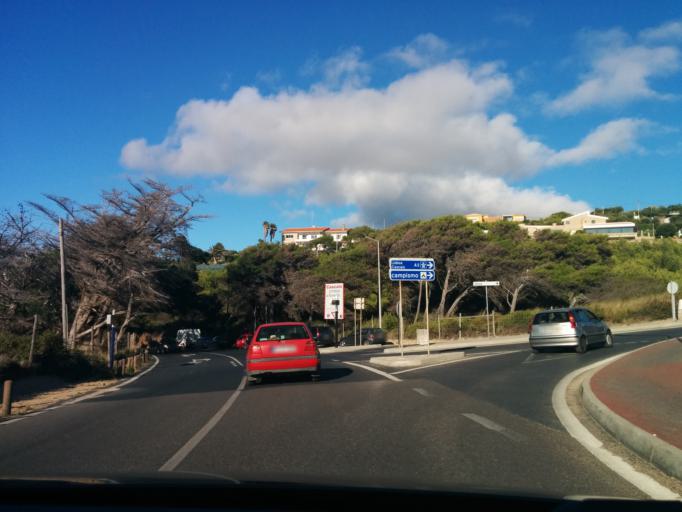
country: PT
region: Lisbon
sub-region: Cascais
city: Cascais
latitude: 38.7302
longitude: -9.4697
